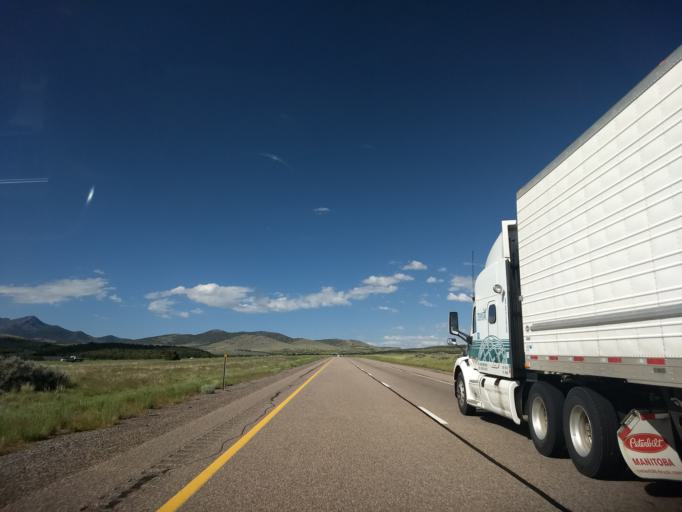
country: US
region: Utah
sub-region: Millard County
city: Fillmore
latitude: 39.1668
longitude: -112.2169
